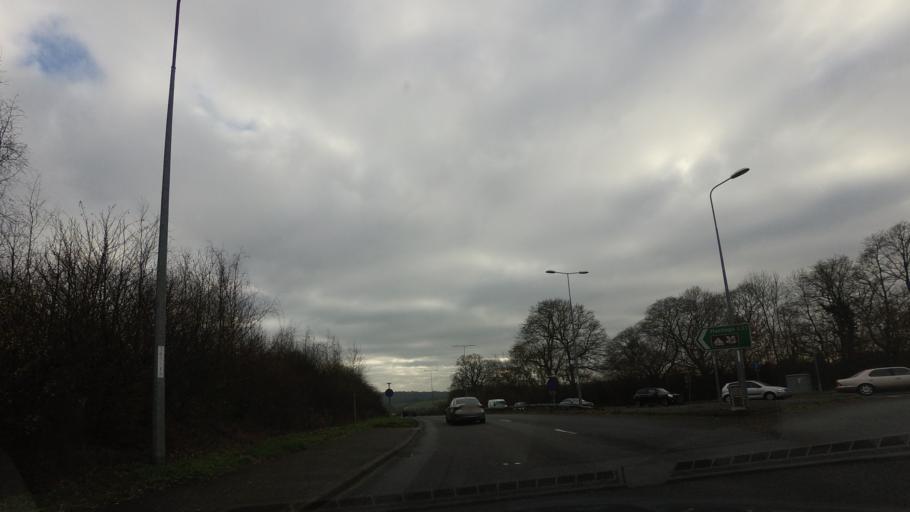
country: GB
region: England
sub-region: Kent
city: Paddock Wood
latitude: 51.1103
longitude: 0.4018
